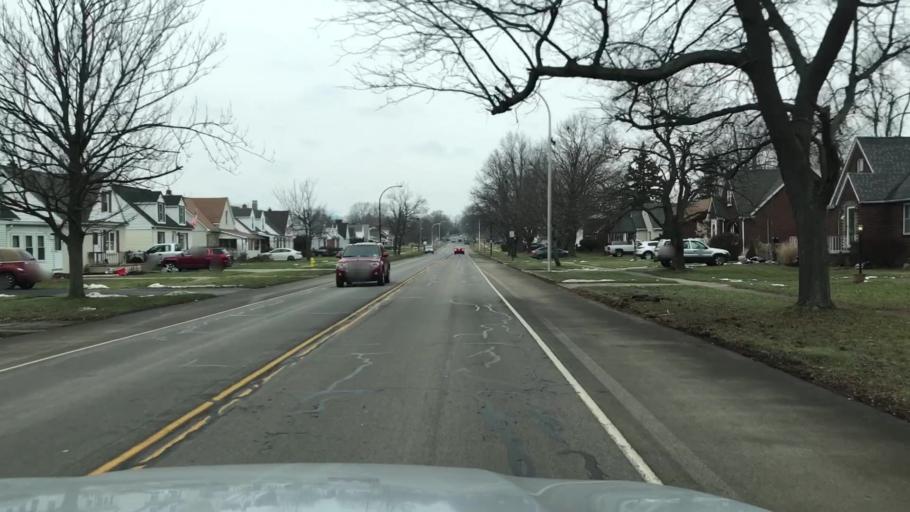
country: US
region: New York
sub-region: Erie County
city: Lackawanna
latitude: 42.8222
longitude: -78.8101
